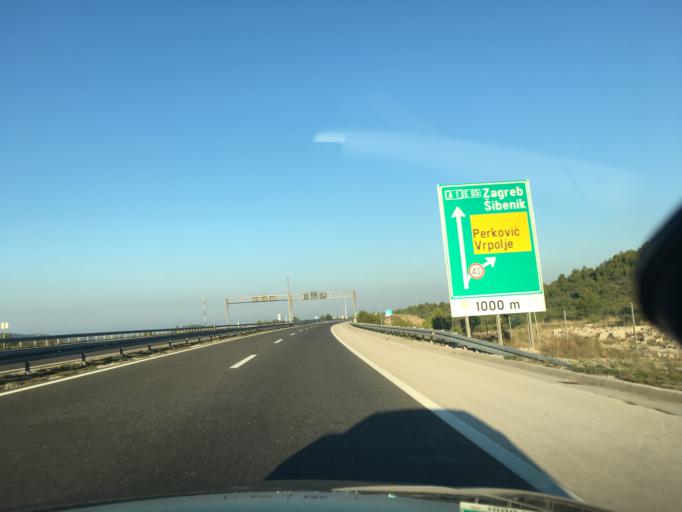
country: HR
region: Sibensko-Kniniska
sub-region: Grad Sibenik
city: Brodarica
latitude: 43.6824
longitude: 16.0750
